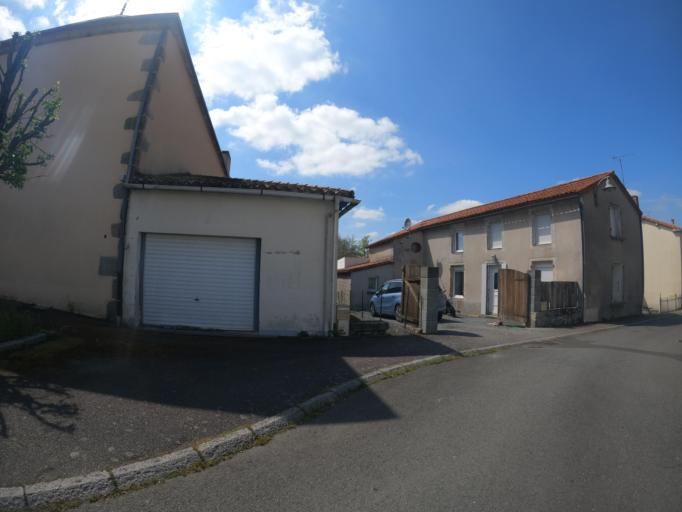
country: FR
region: Poitou-Charentes
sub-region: Departement des Deux-Sevres
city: La Chapelle-Saint-Laurent
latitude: 46.6941
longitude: -0.5004
